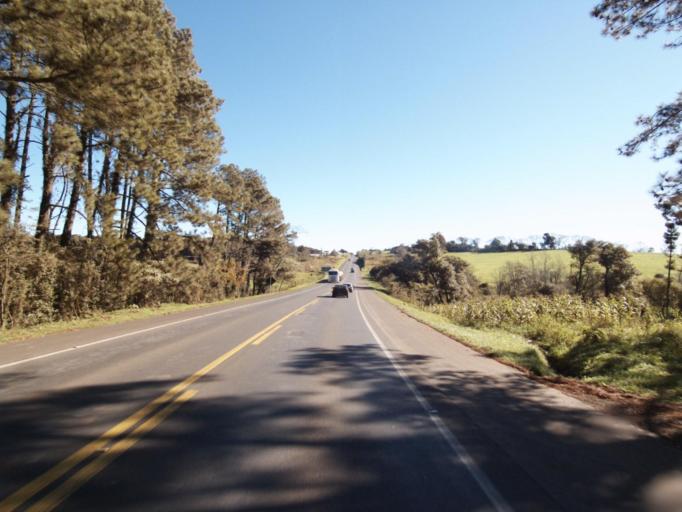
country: BR
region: Santa Catarina
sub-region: Xanxere
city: Xanxere
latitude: -26.9145
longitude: -52.4787
